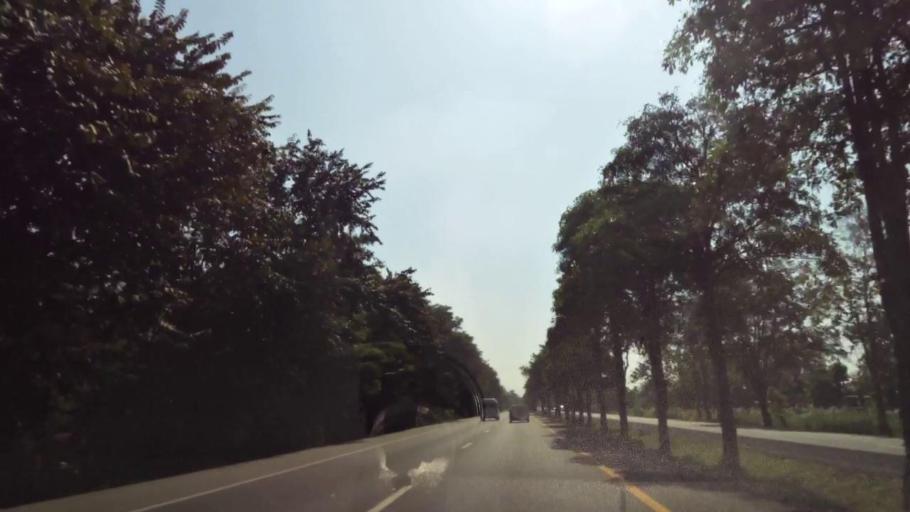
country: TH
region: Phichit
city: Bueng Na Rang
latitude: 16.0704
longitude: 100.1238
